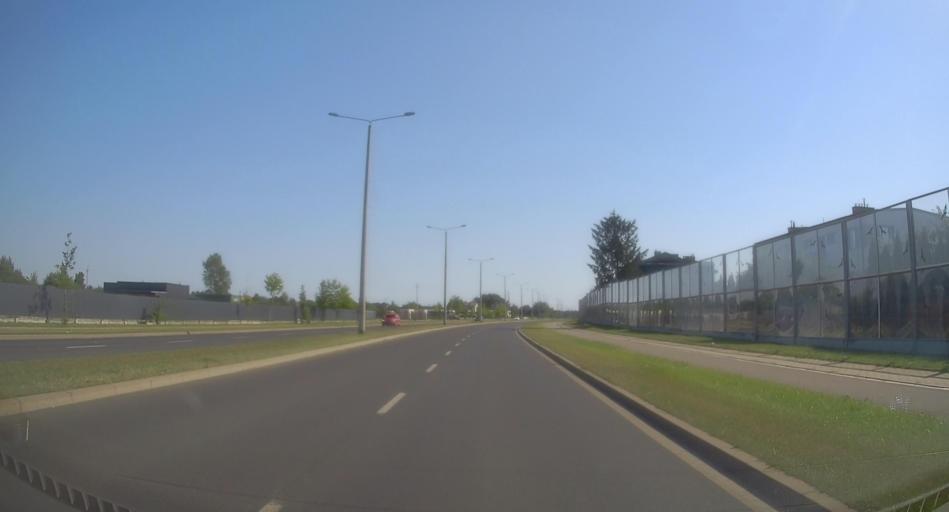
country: PL
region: Lodz Voivodeship
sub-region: Skierniewice
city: Skierniewice
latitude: 51.9512
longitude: 20.1590
